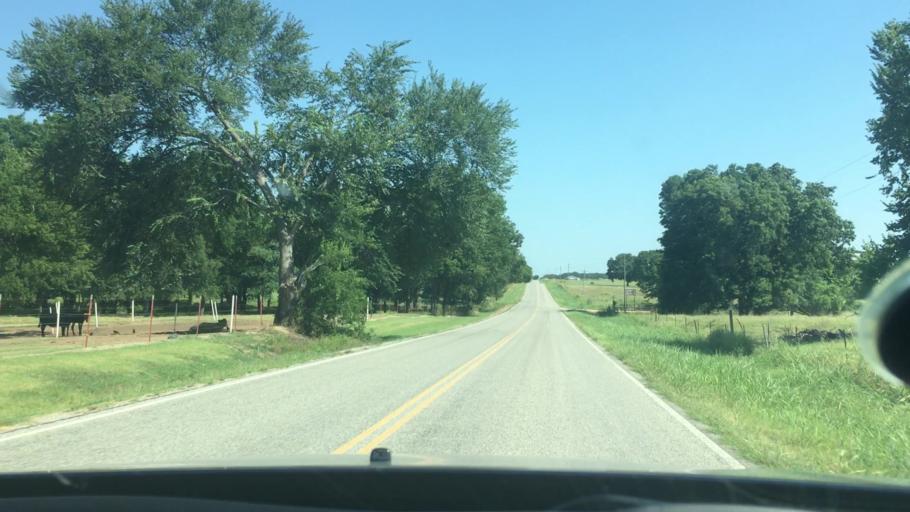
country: US
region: Oklahoma
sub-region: Johnston County
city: Tishomingo
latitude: 34.3019
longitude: -96.6185
